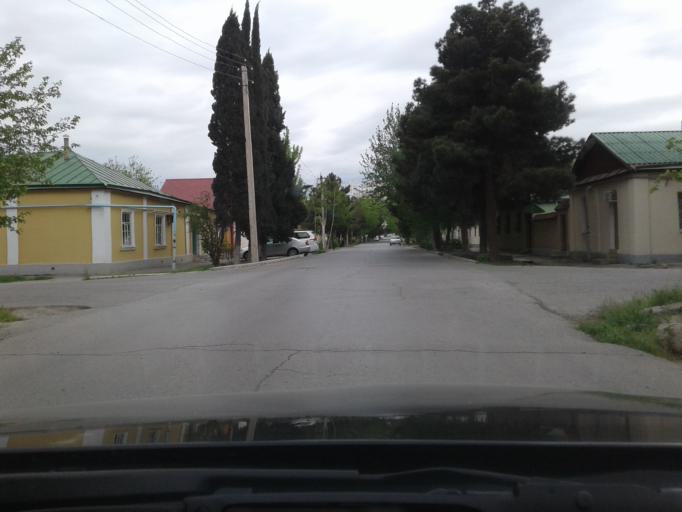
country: TM
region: Ahal
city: Ashgabat
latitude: 37.9478
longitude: 58.3576
